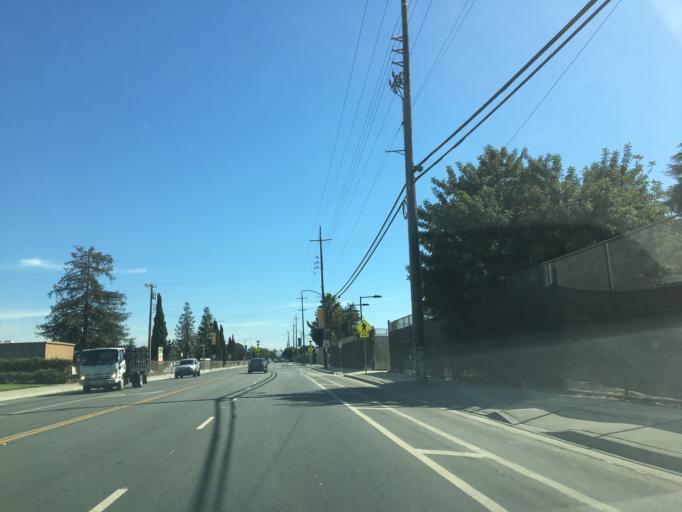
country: US
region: California
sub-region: Santa Clara County
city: San Jose
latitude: 37.3226
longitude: -121.8676
